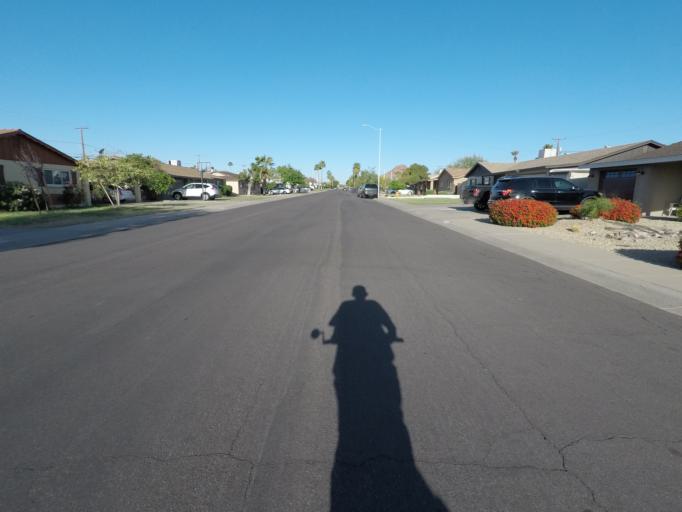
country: US
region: Arizona
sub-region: Maricopa County
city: Tempe Junction
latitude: 33.4620
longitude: -111.9328
